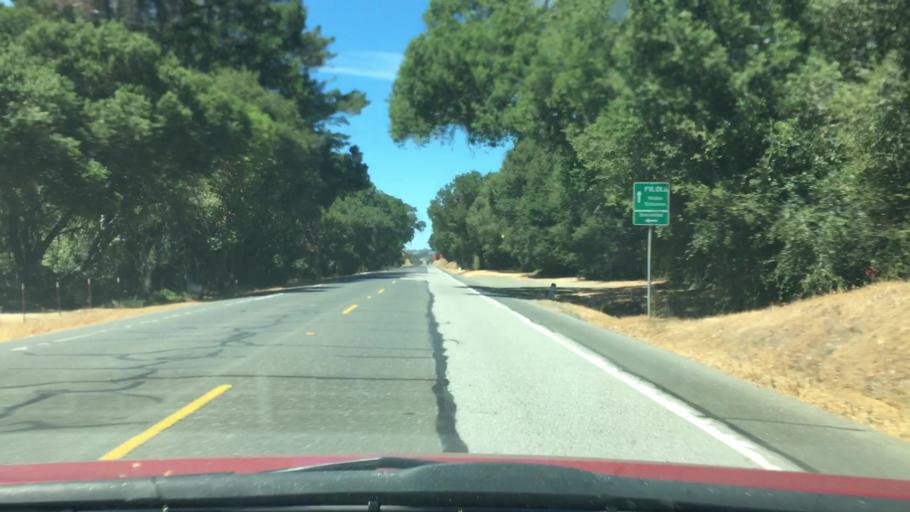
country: US
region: California
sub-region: San Mateo County
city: Emerald Lake Hills
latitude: 37.4679
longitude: -122.3016
